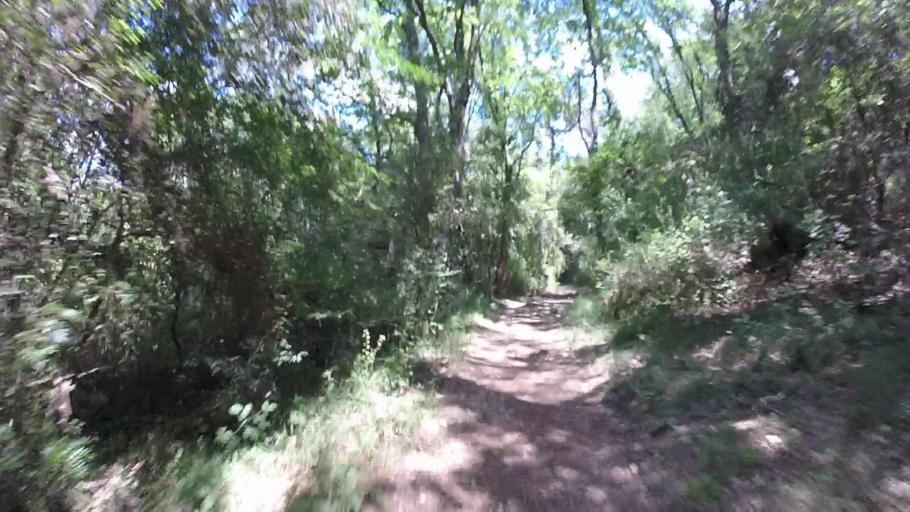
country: FR
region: Provence-Alpes-Cote d'Azur
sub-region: Departement des Alpes-Maritimes
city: Vallauris
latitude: 43.6099
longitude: 7.0398
